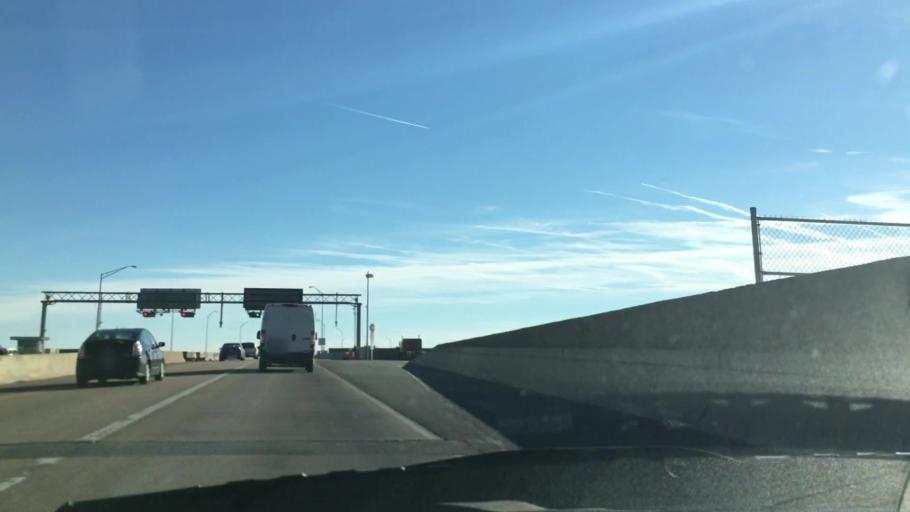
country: US
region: Virginia
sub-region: City of Newport News
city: Newport News
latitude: 36.9449
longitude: -76.4038
